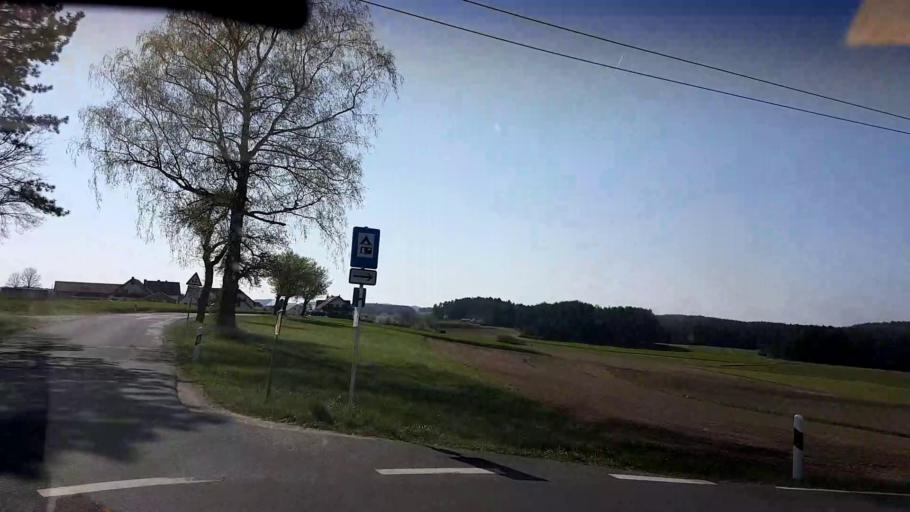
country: DE
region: Bavaria
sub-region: Upper Franconia
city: Pottenstein
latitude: 49.7902
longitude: 11.3842
